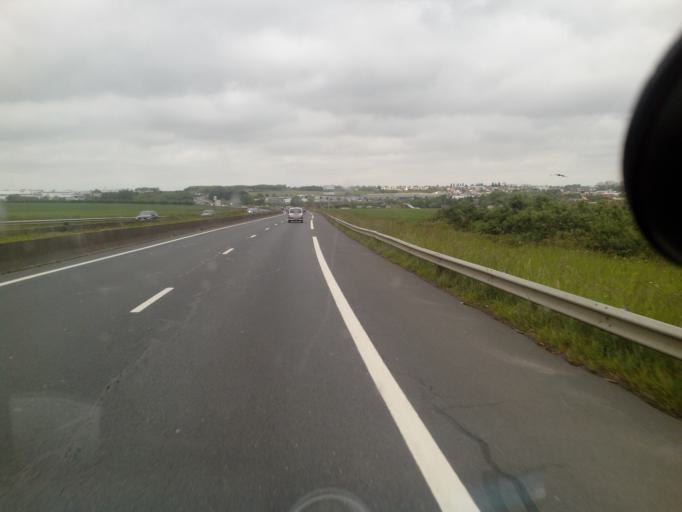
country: FR
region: Lower Normandy
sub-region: Departement du Calvados
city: Bretteville-sur-Odon
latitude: 49.1761
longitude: -0.4290
